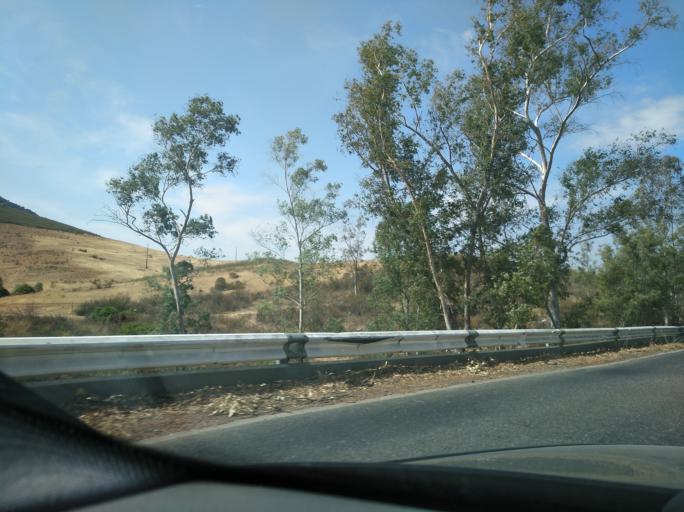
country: PT
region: Beja
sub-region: Mertola
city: Mertola
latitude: 37.6974
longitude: -7.7441
